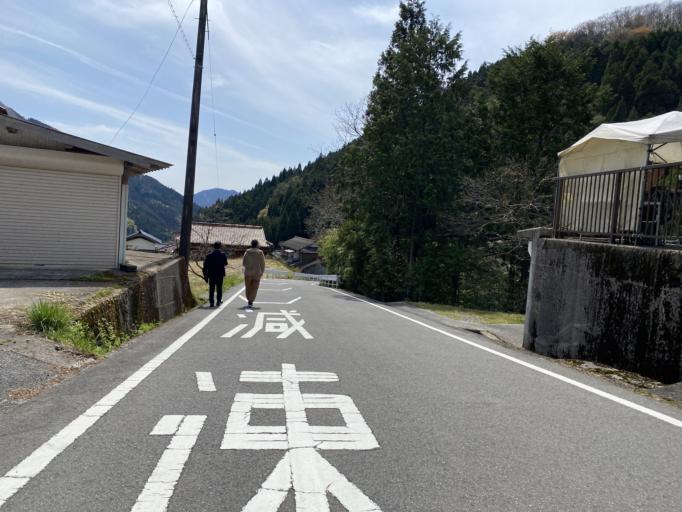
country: JP
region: Hyogo
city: Yamazakicho-nakabirose
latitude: 35.1753
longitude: 134.3529
